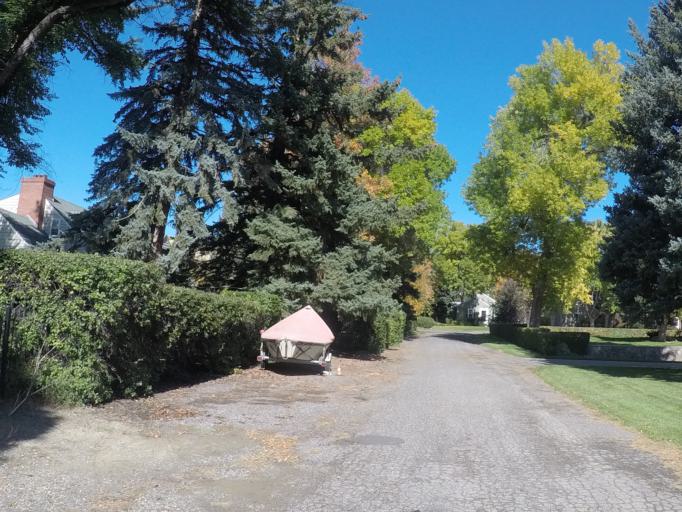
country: US
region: Montana
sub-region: Yellowstone County
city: Billings
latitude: 45.7962
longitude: -108.5336
